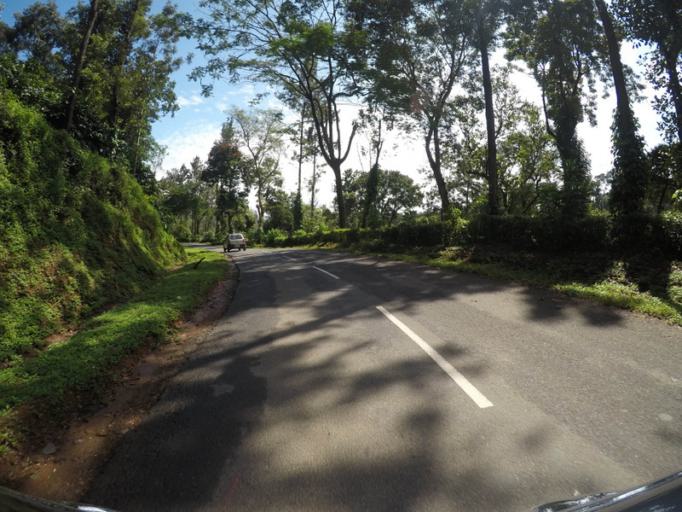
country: IN
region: Karnataka
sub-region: Kodagu
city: Suntikoppa
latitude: 12.4808
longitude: 75.7908
